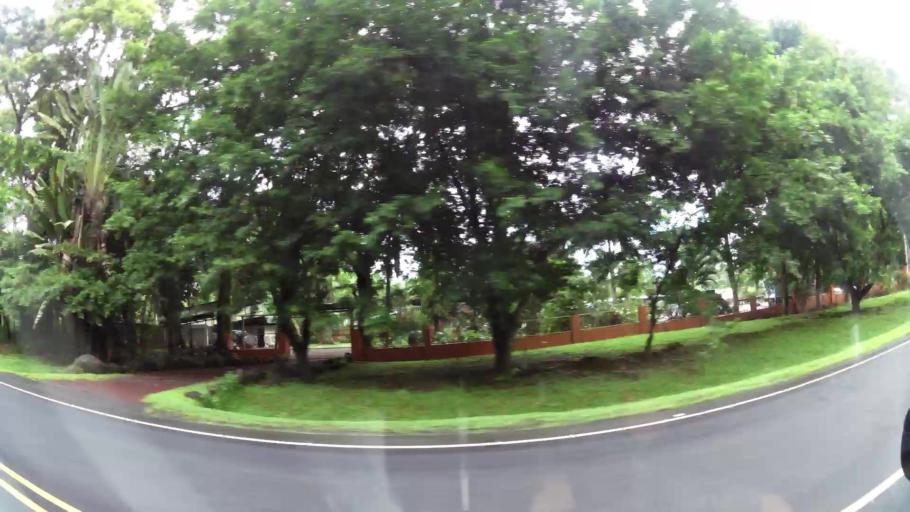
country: CR
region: Limon
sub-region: Canton de Guacimo
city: Guacimo
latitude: 10.2086
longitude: -83.7013
